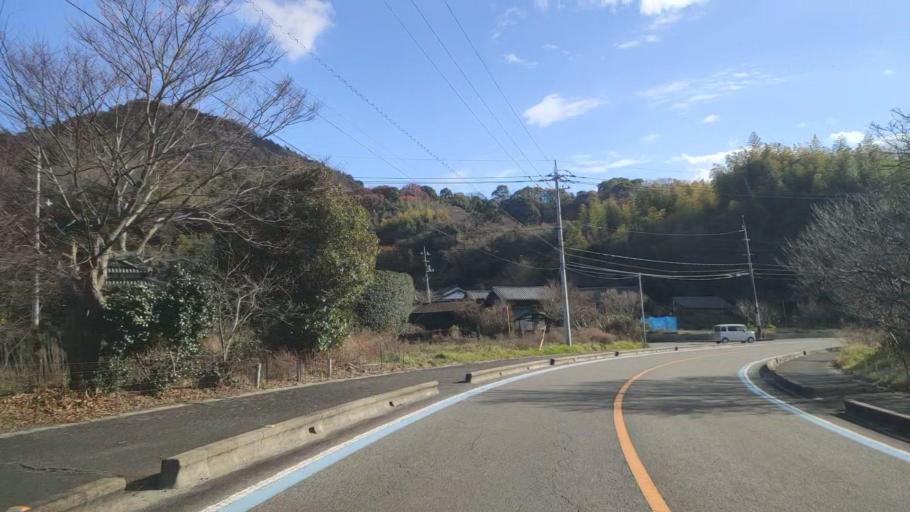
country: JP
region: Hiroshima
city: Innoshima
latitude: 34.2209
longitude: 133.0683
